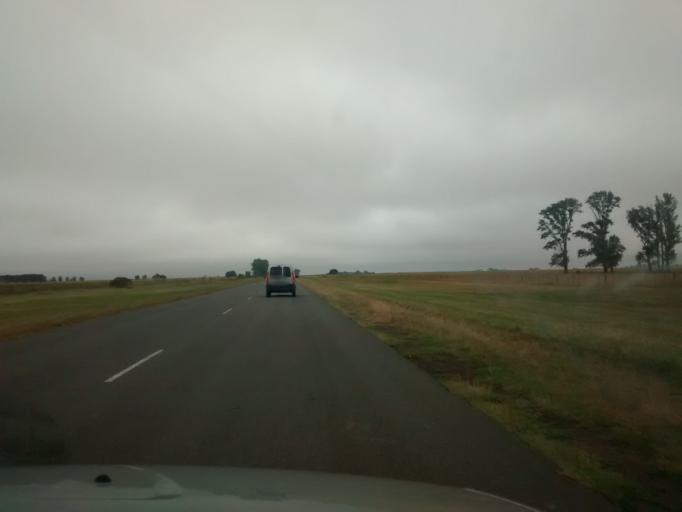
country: AR
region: Buenos Aires
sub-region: Partido de Ayacucho
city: Ayacucho
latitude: -37.2317
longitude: -58.4940
